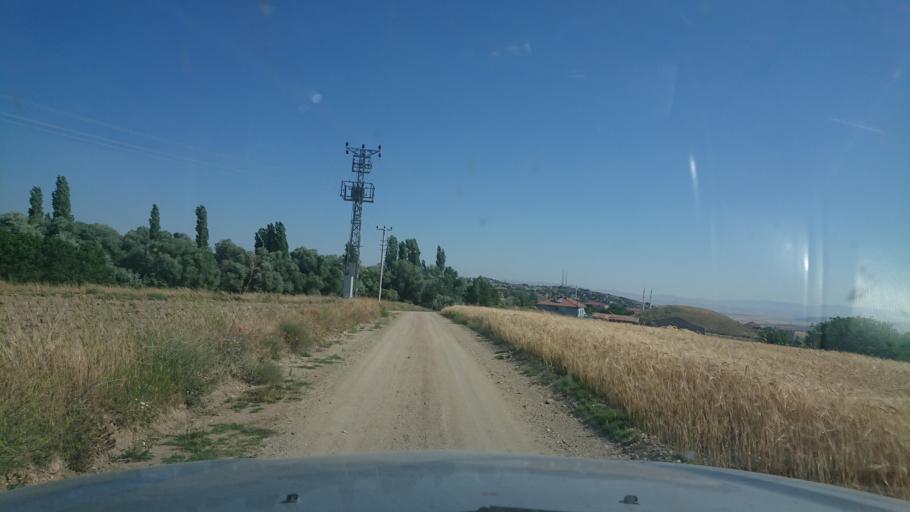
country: TR
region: Aksaray
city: Agacoren
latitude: 38.8604
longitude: 33.9122
